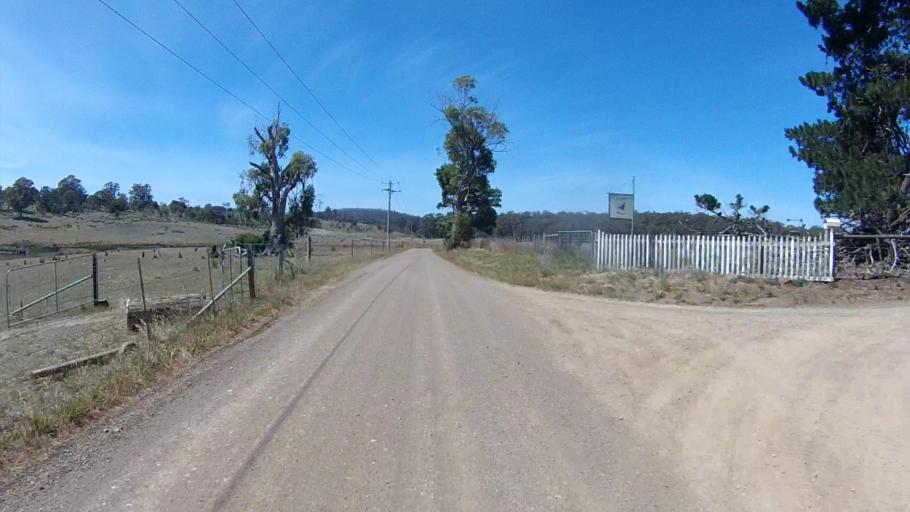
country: AU
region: Tasmania
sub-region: Sorell
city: Sorell
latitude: -42.7757
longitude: 147.6531
